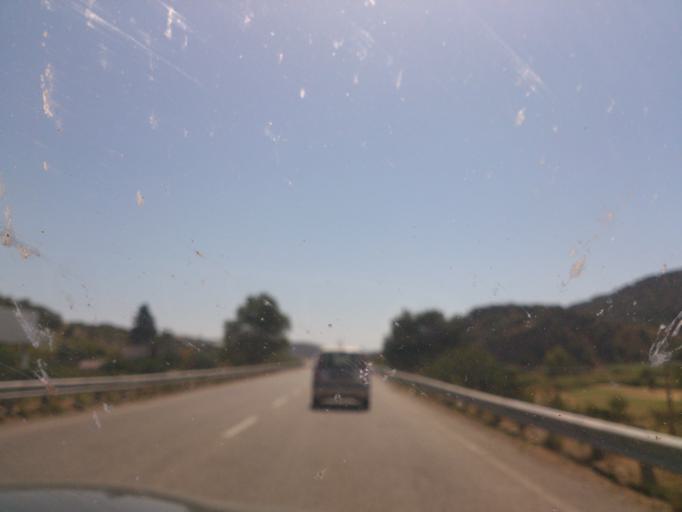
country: IT
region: Calabria
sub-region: Provincia di Reggio Calabria
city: Stilo
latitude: 38.4652
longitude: 16.4966
